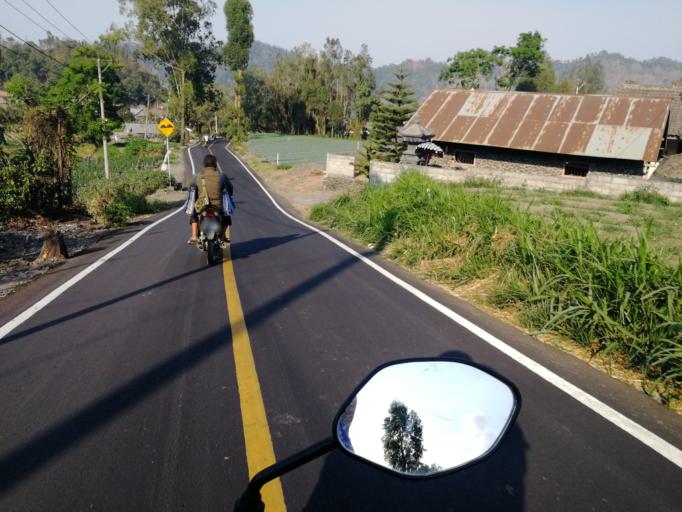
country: ID
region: Bali
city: Banjar Trunyan
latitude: -8.2432
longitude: 115.4015
